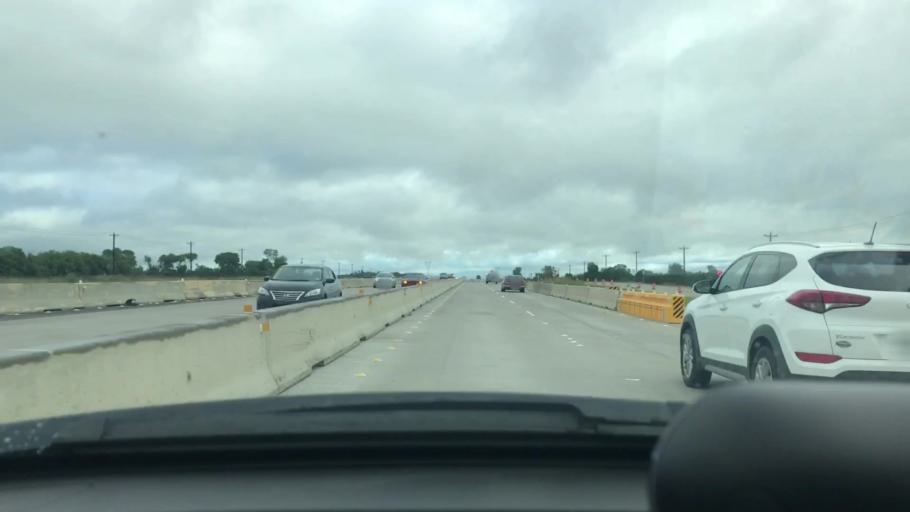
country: US
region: Texas
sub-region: Collin County
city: Anna
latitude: 33.3531
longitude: -96.5850
